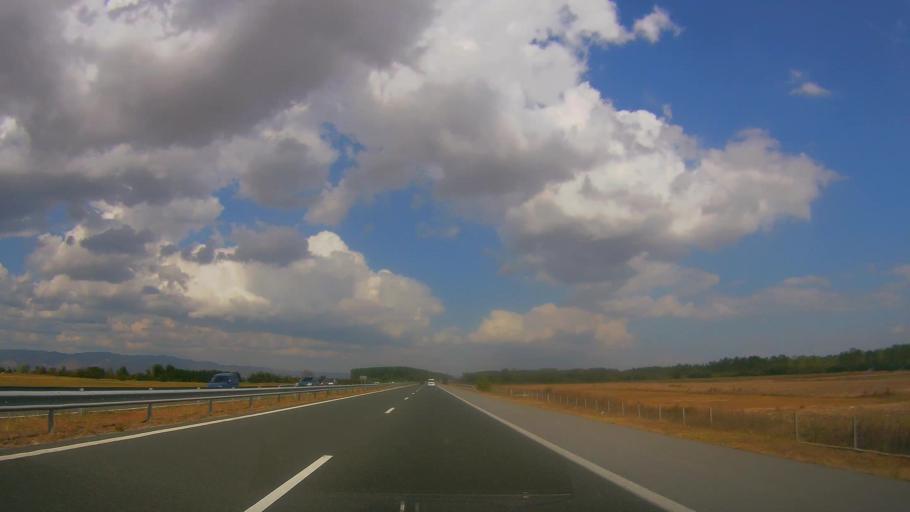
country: BG
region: Yambol
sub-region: Obshtina Yambol
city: Yambol
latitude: 42.5445
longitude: 26.4914
